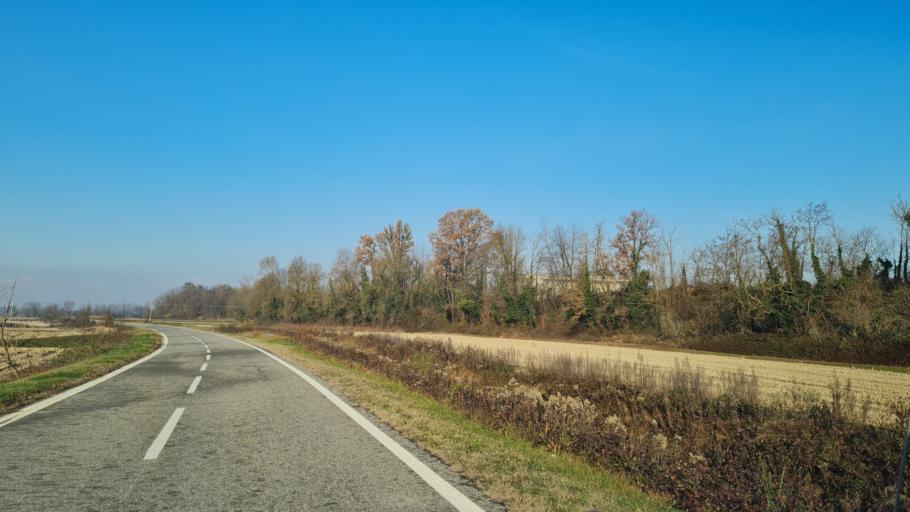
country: IT
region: Piedmont
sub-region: Provincia di Vercelli
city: Villarboit
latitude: 45.4407
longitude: 8.3293
